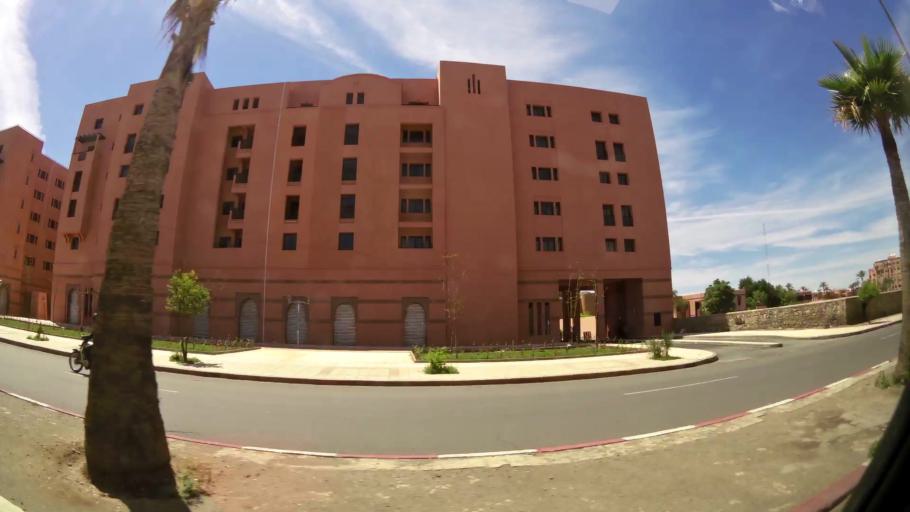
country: MA
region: Marrakech-Tensift-Al Haouz
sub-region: Marrakech
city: Marrakesh
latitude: 31.6509
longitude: -8.0011
